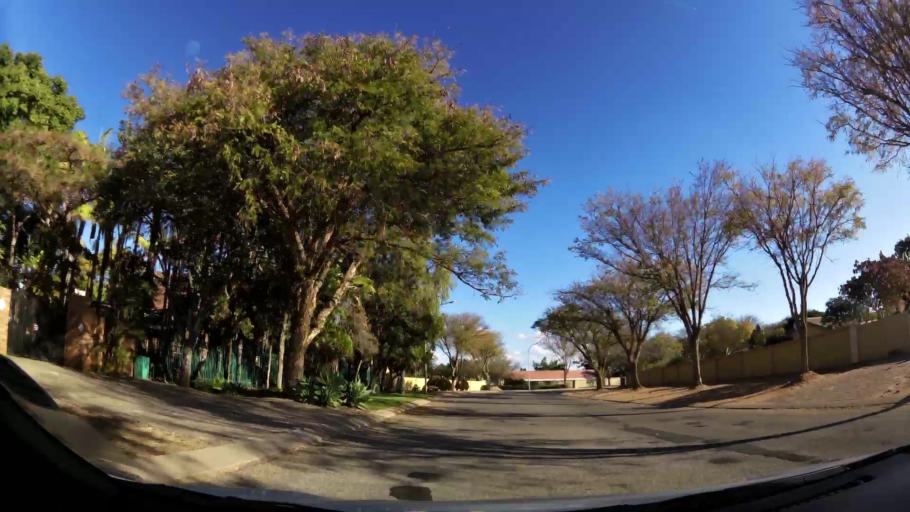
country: ZA
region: Limpopo
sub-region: Capricorn District Municipality
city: Polokwane
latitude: -23.8904
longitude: 29.4859
